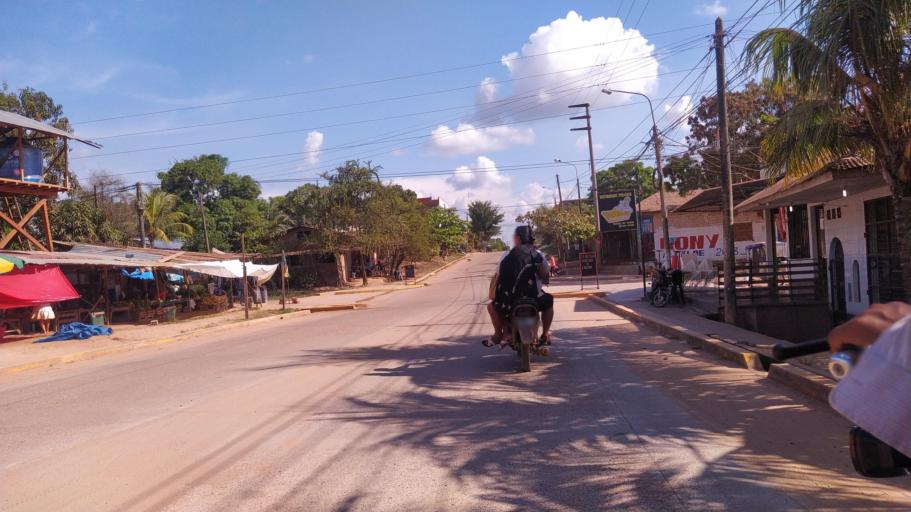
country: PE
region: Ucayali
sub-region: Provincia de Coronel Portillo
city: Puerto Callao
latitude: -8.3566
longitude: -74.5804
